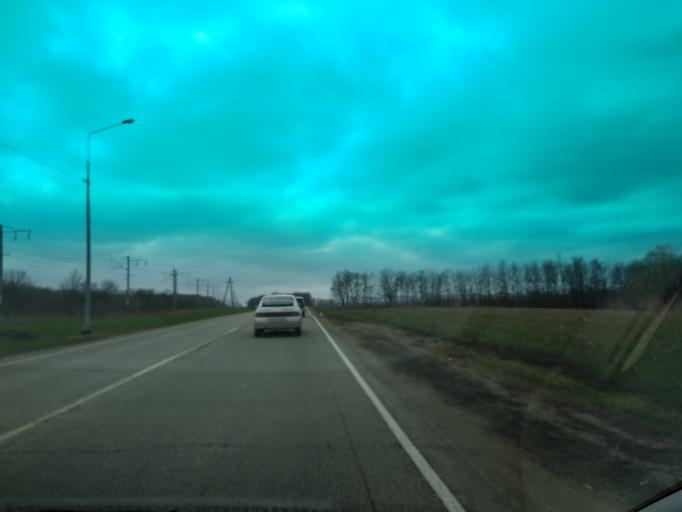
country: RU
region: Krasnodarskiy
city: Novorozhdestvenskaya
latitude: 45.8025
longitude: 39.9860
